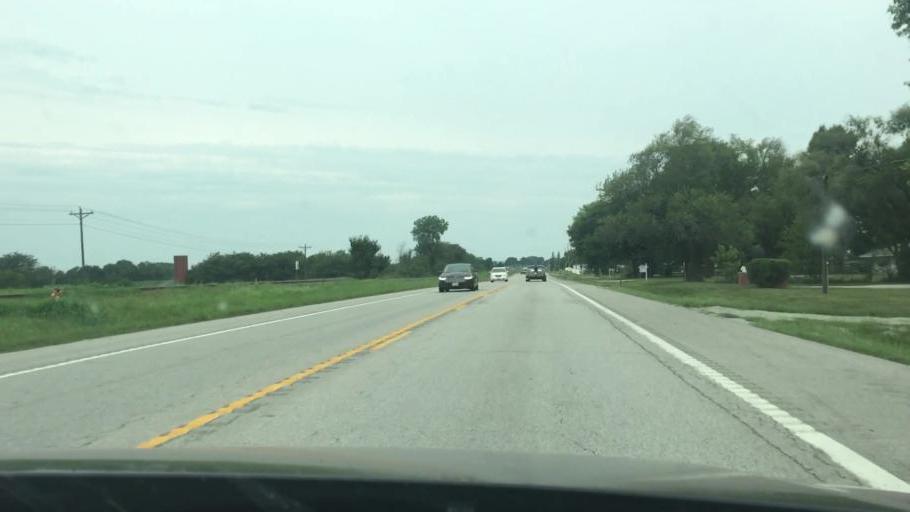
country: US
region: Missouri
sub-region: Pettis County
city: Sedalia
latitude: 38.6956
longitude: -93.1596
